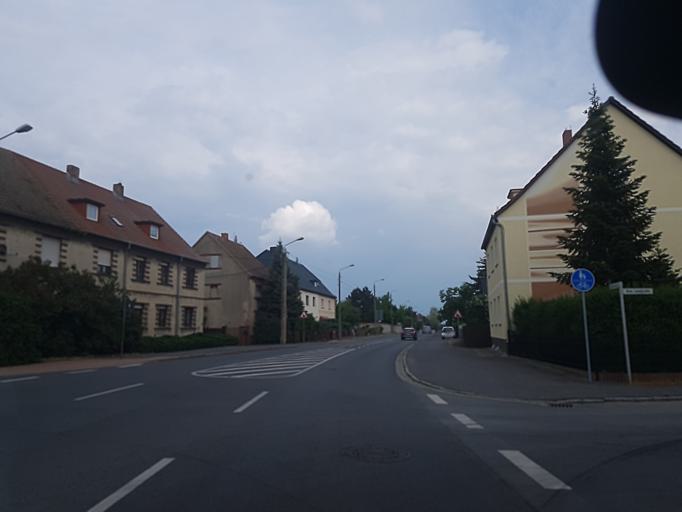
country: DE
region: Saxony-Anhalt
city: Wittenburg
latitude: 51.8768
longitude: 12.6065
